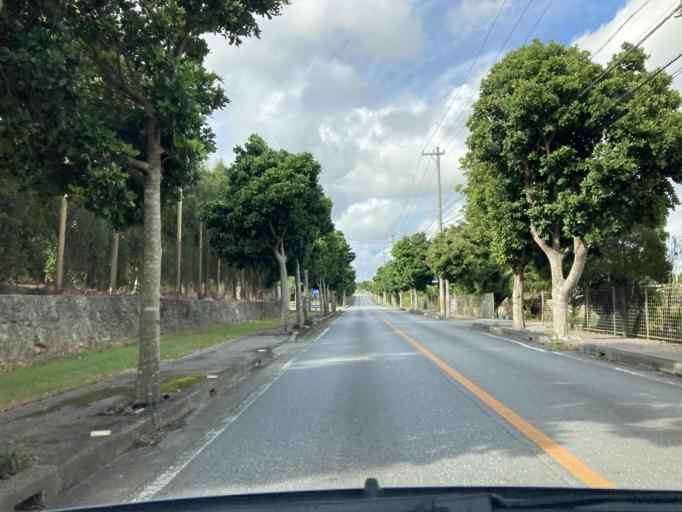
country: JP
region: Okinawa
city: Itoman
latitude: 26.1158
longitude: 127.7169
